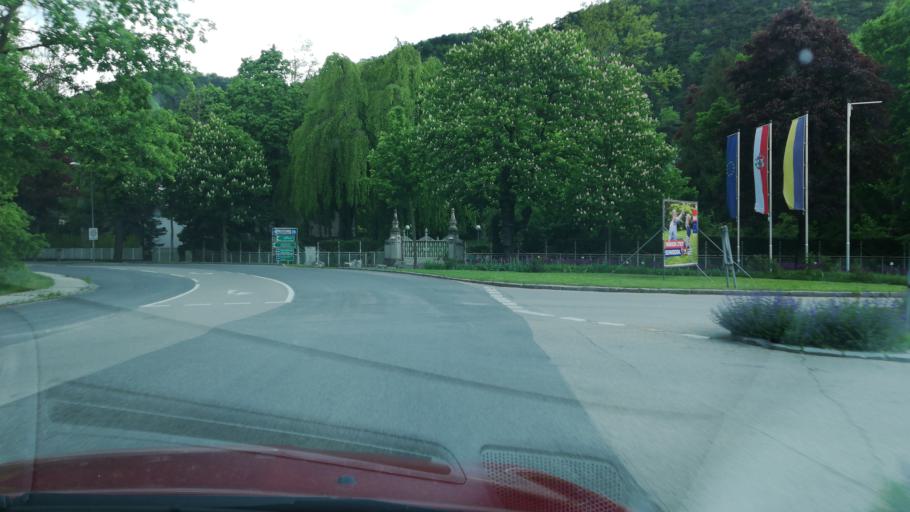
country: AT
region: Lower Austria
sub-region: Politischer Bezirk Baden
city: Baden
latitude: 48.0095
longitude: 16.2082
